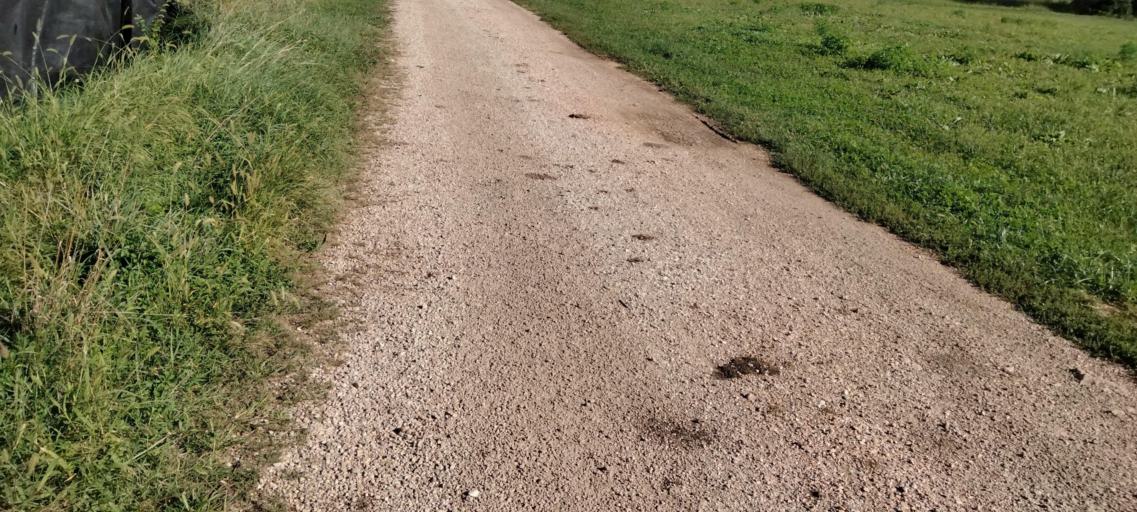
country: IT
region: Veneto
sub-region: Provincia di Vicenza
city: Creazzo
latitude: 45.5260
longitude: 11.4811
